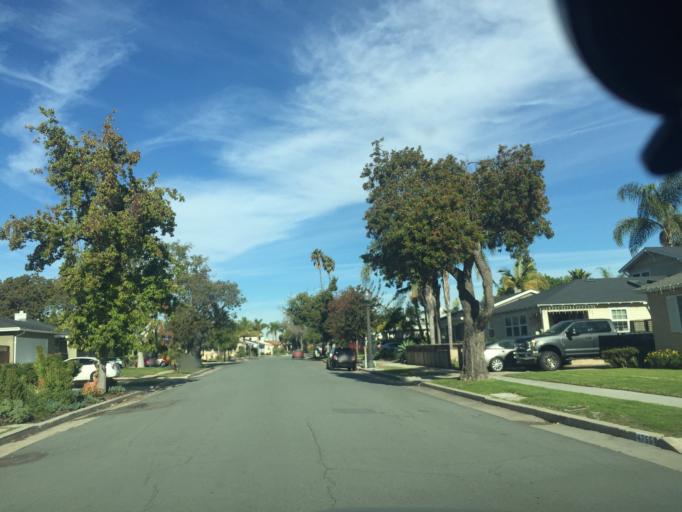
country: US
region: California
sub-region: San Diego County
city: Lemon Grove
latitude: 32.7640
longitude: -117.0852
